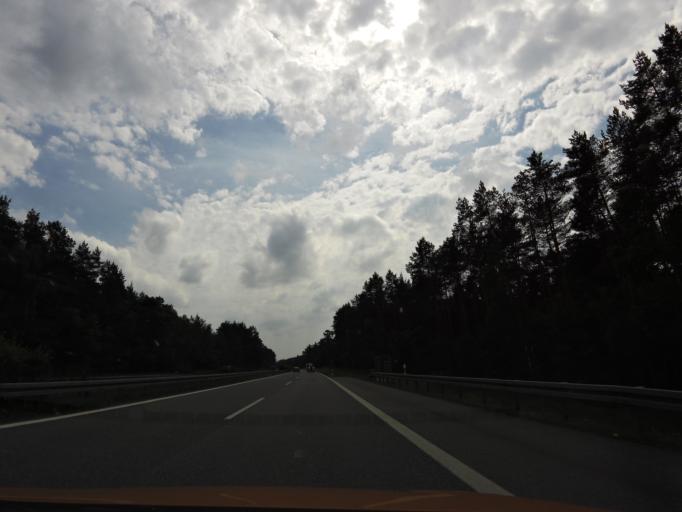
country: DE
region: Mecklenburg-Vorpommern
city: Mirow
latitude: 53.5300
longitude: 11.4667
